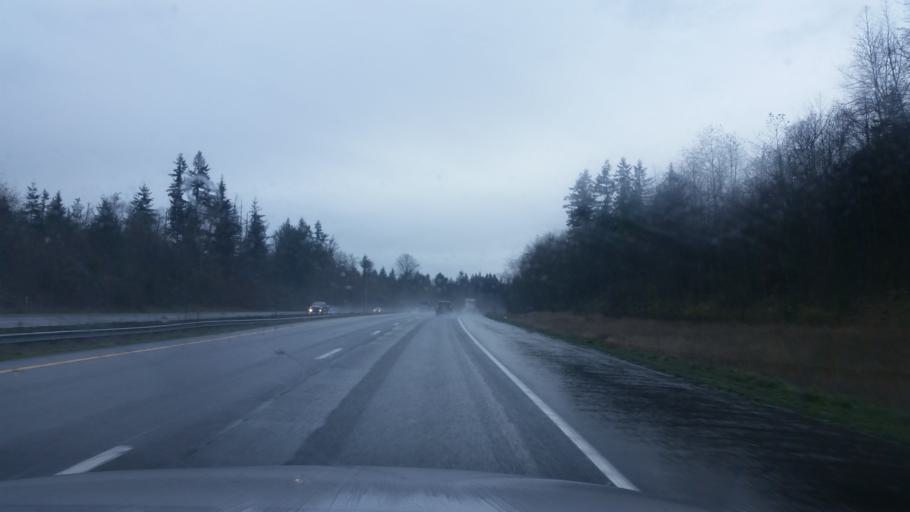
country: US
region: Washington
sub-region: King County
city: Hobart
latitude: 47.4269
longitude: -121.9909
